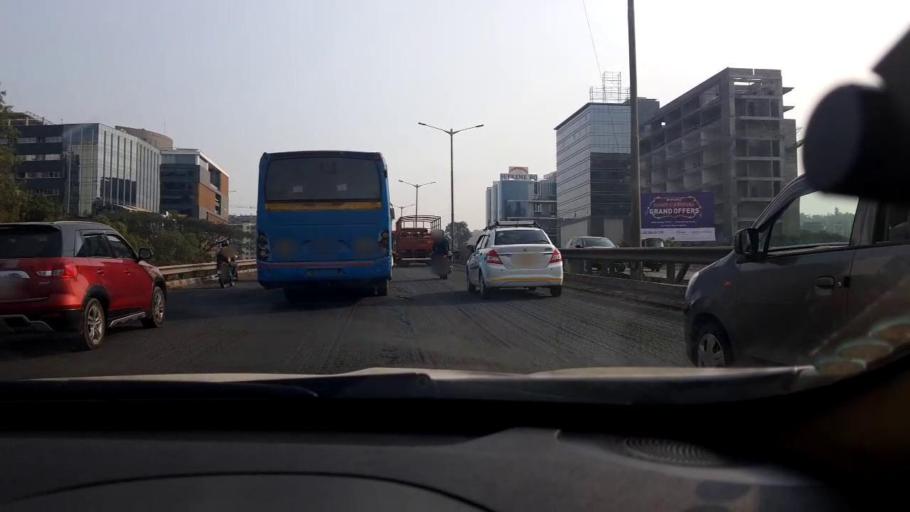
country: IN
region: Maharashtra
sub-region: Pune Division
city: Pimpri
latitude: 18.5554
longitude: 73.7708
